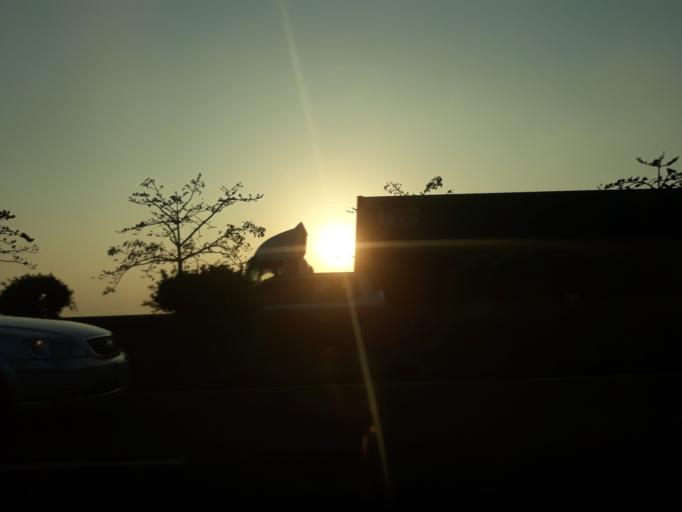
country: TW
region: Taiwan
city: Fengshan
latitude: 22.7699
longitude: 120.3273
